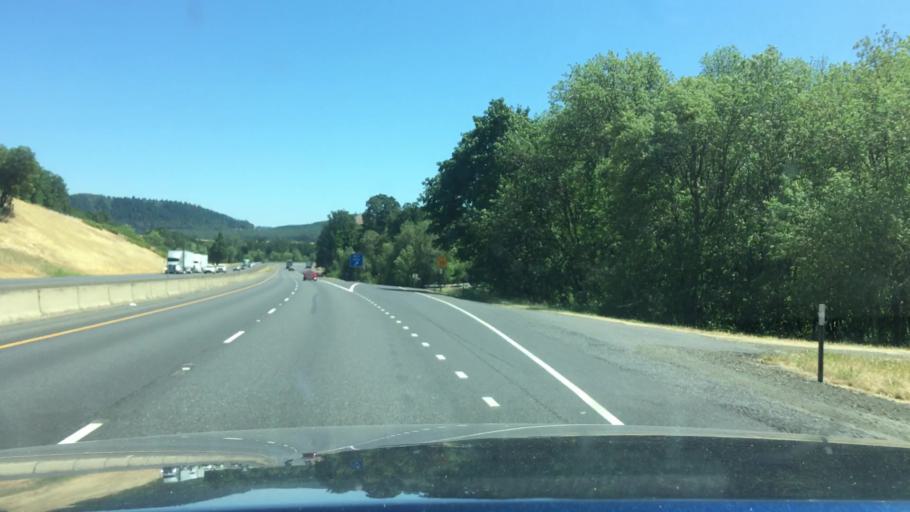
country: US
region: Oregon
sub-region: Douglas County
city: Sutherlin
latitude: 43.4789
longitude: -123.3219
